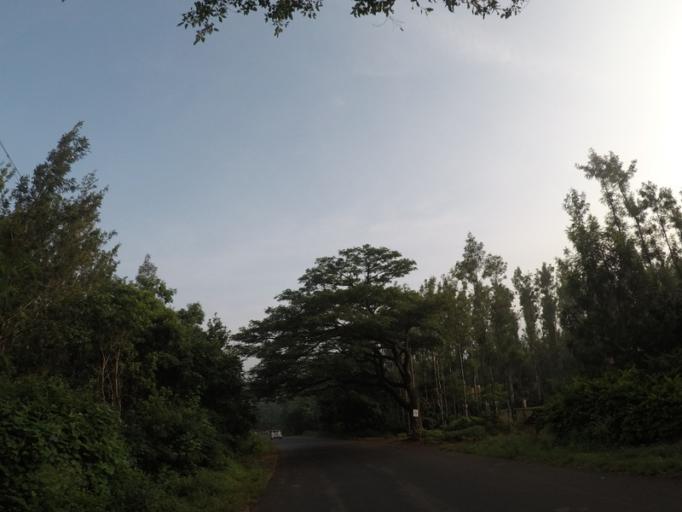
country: IN
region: Karnataka
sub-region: Chikmagalur
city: Chikmagalur
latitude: 13.4055
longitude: 75.7966
